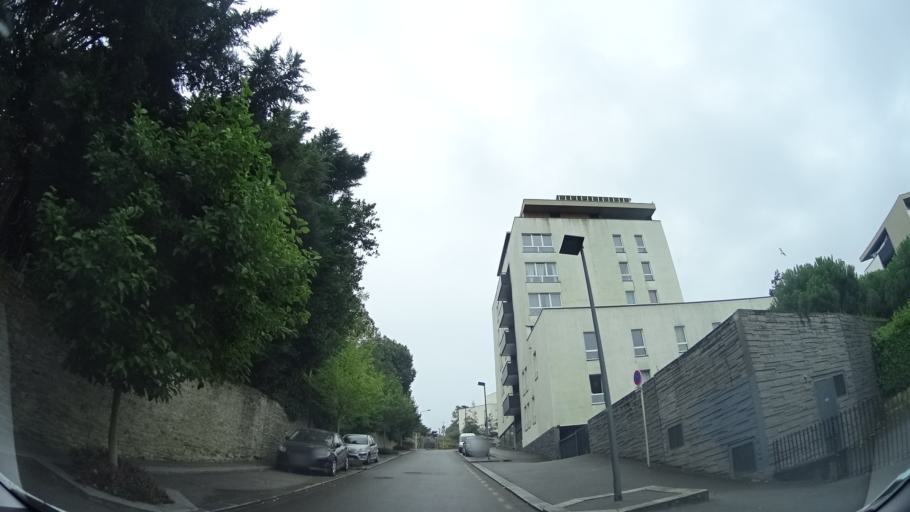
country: FR
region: Lower Normandy
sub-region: Departement de la Manche
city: Cherbourg-Octeville
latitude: 49.6320
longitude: -1.6214
